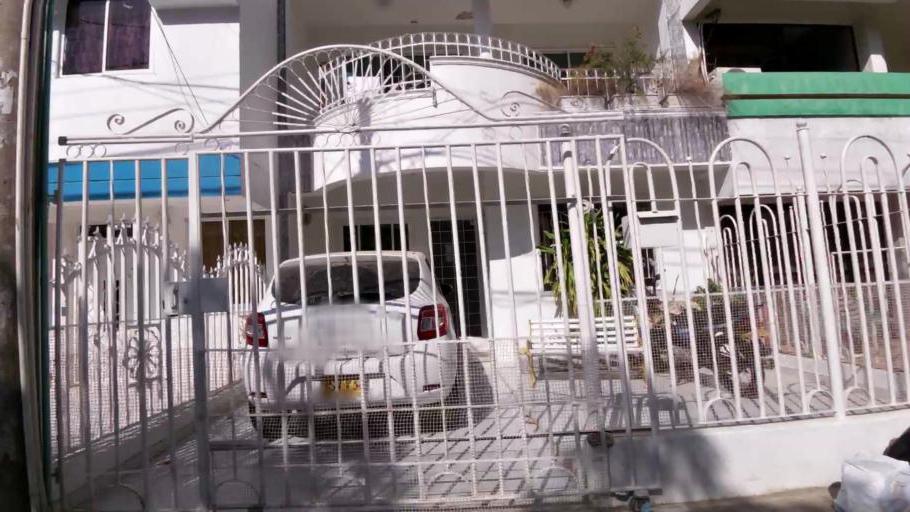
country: CO
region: Bolivar
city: Cartagena
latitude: 10.3821
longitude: -75.4779
